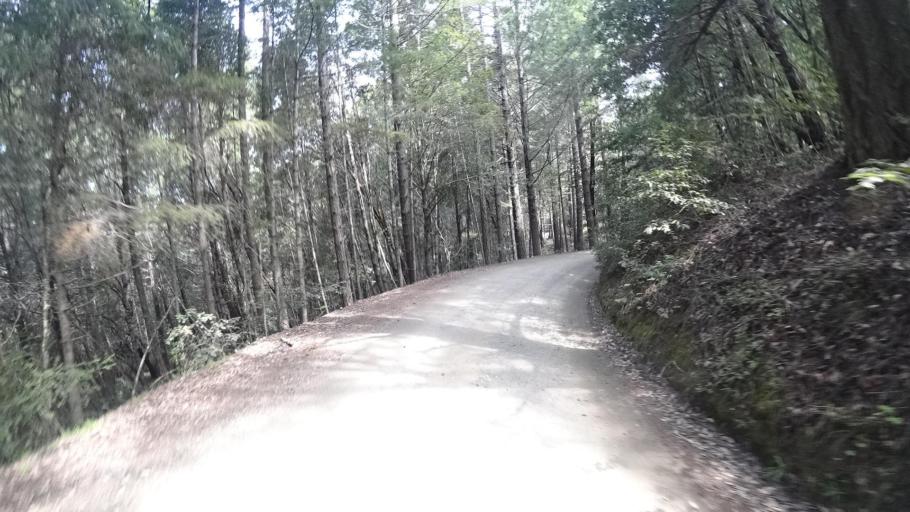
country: US
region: California
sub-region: Humboldt County
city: Redway
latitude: 40.0278
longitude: -123.8420
